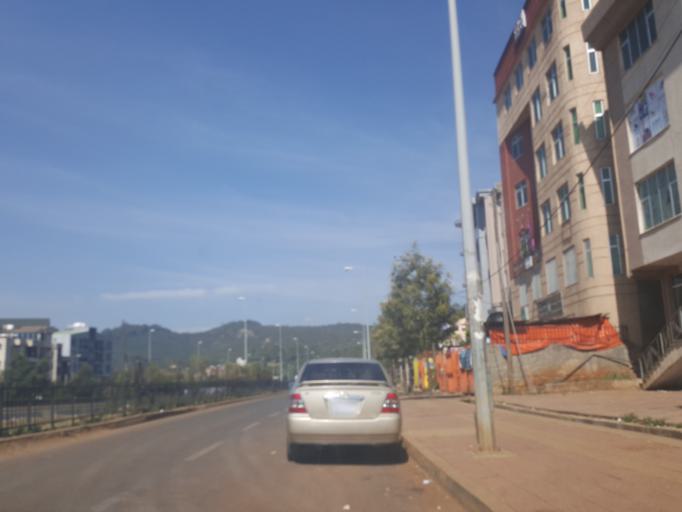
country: ET
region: Adis Abeba
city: Addis Ababa
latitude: 9.0665
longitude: 38.7268
